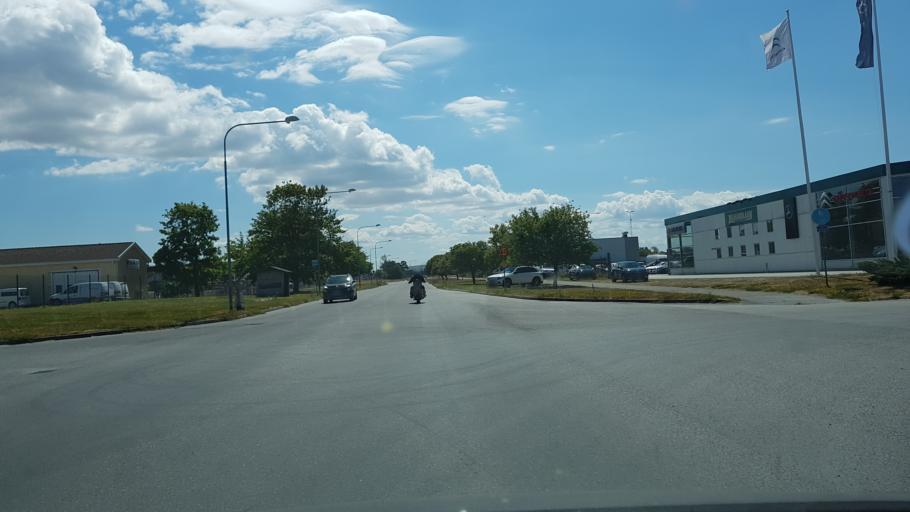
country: SE
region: Gotland
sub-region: Gotland
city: Visby
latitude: 57.6445
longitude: 18.3267
